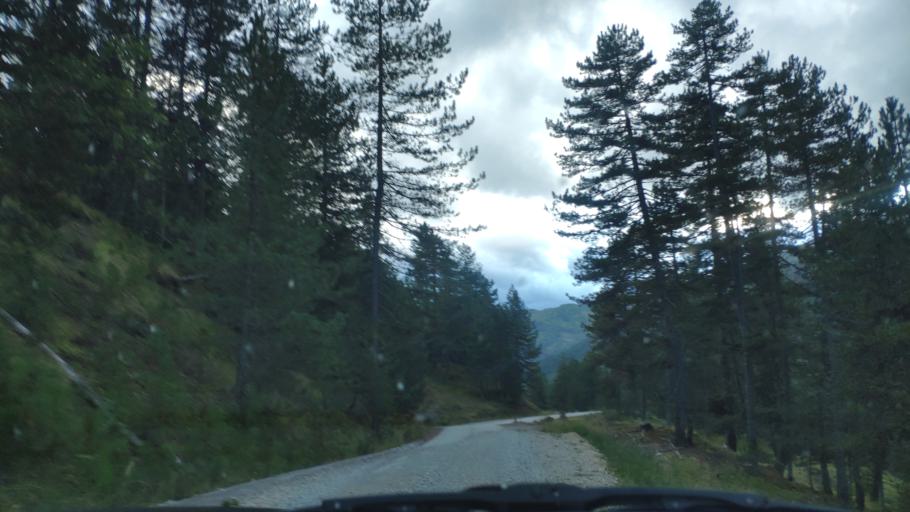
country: AL
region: Korce
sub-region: Rrethi i Kolonjes
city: Erseke
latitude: 40.2865
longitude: 20.8636
